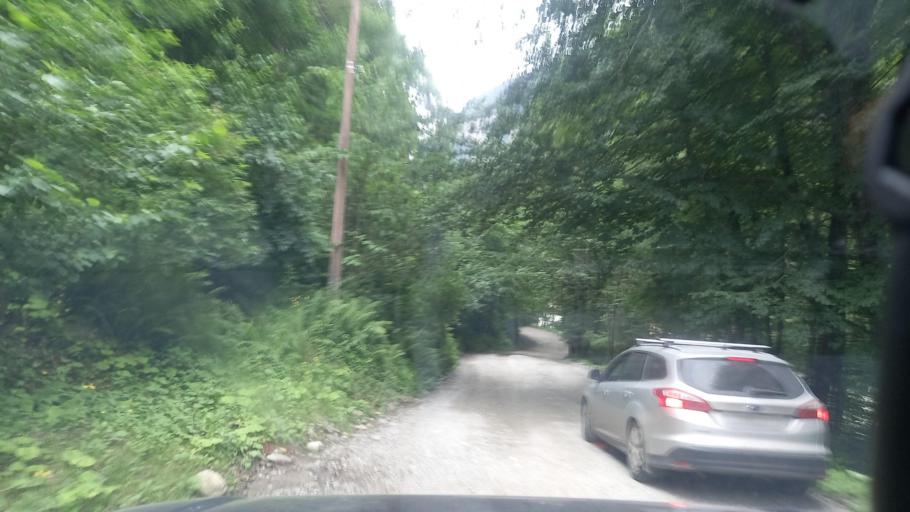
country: RU
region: Karachayevo-Cherkesiya
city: Kurdzhinovo
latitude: 43.8653
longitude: 40.9413
